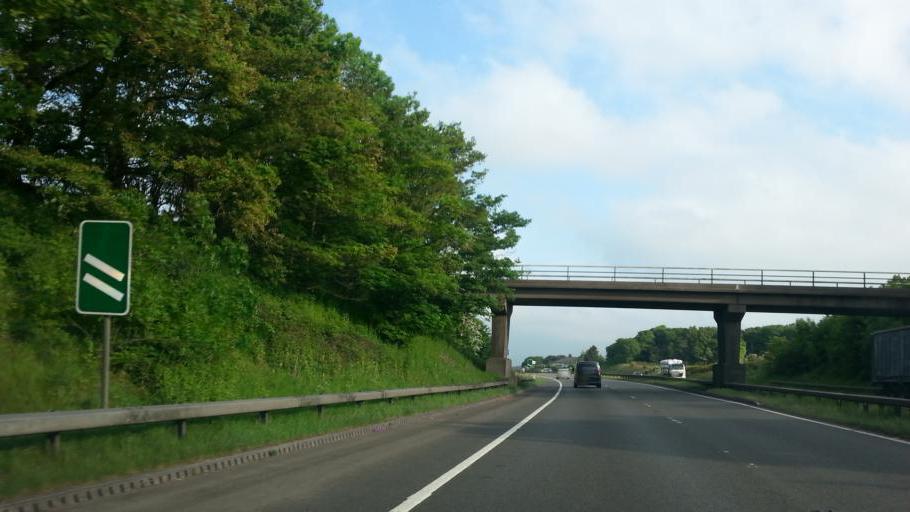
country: GB
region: England
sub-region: Nottinghamshire
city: Bircotes
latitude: 53.3835
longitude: -1.0568
